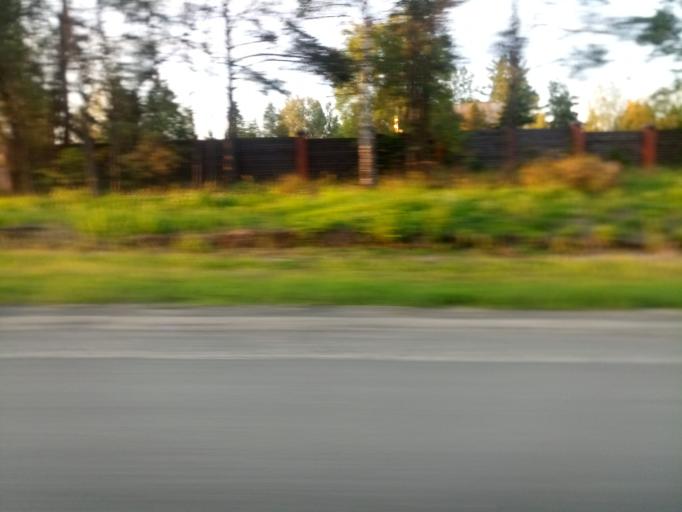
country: RU
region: Moskovskaya
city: Noginsk-9
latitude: 56.1076
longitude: 38.6252
